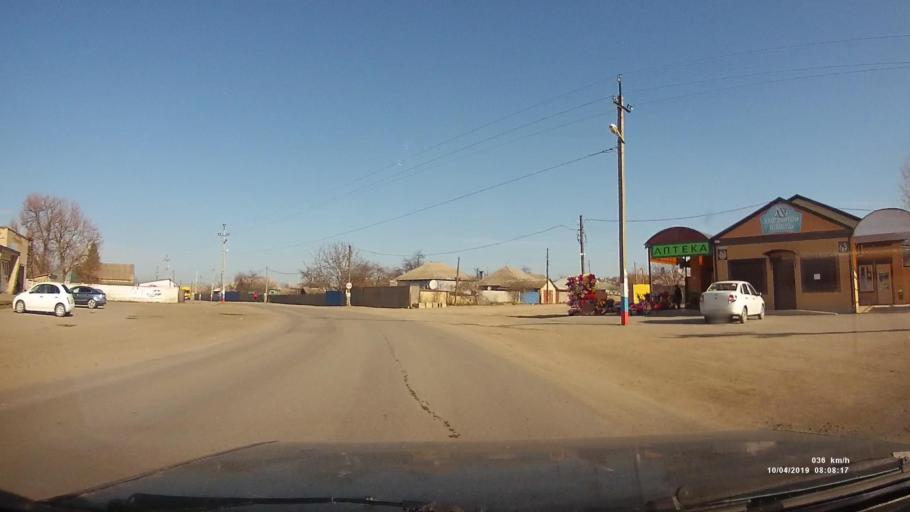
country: RU
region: Rostov
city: Staraya Stanitsa
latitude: 48.3476
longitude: 40.2865
